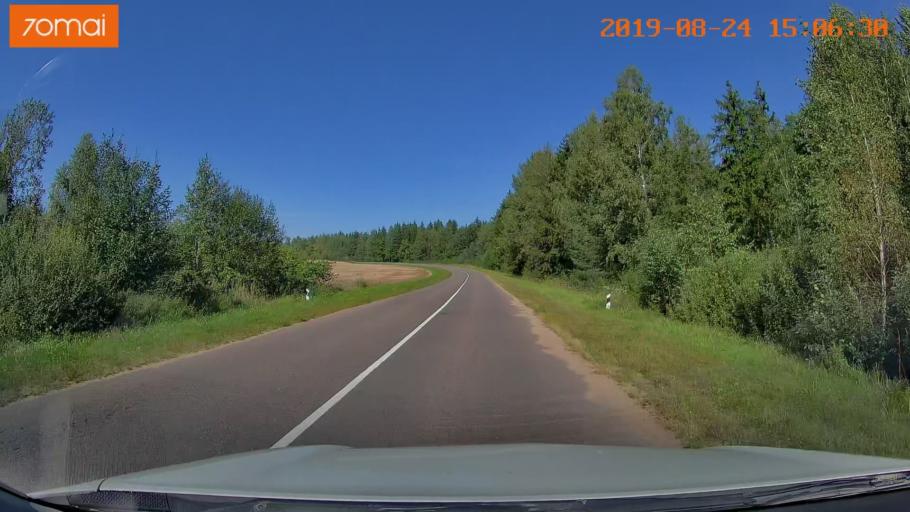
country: BY
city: Michanovichi
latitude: 53.6008
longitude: 27.6781
